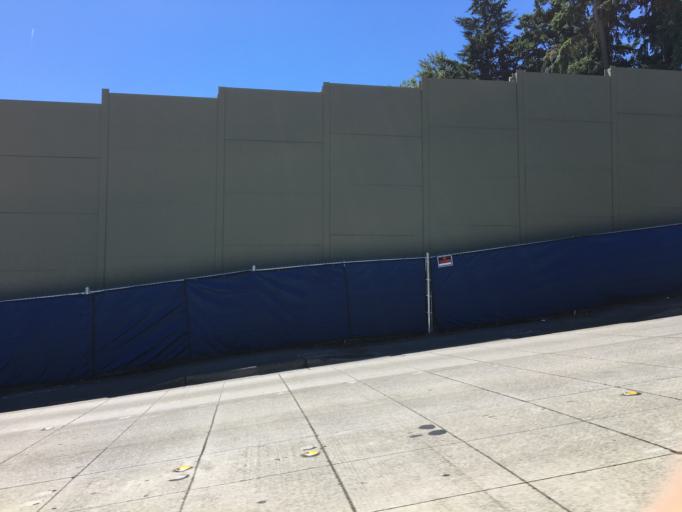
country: US
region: Washington
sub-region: King County
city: Bellevue
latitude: 47.6100
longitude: -122.1919
